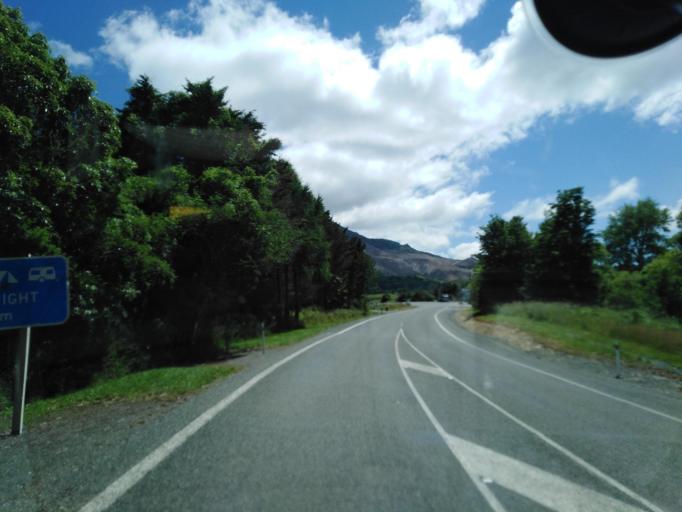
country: NZ
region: Nelson
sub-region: Nelson City
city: Nelson
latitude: -41.2153
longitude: 173.3950
